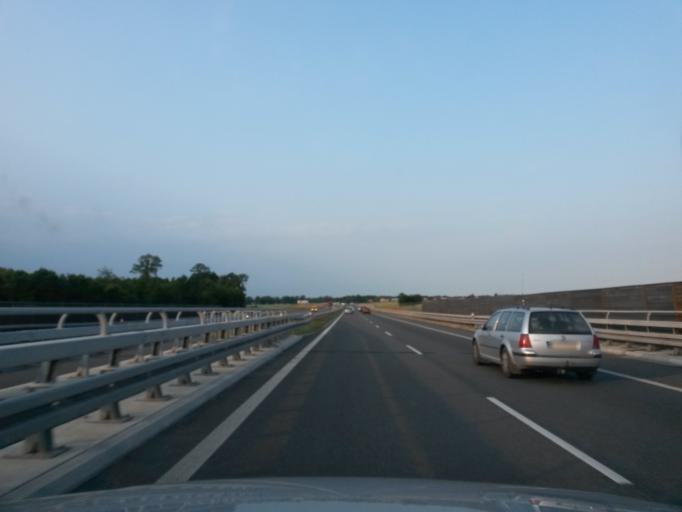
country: PL
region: Lower Silesian Voivodeship
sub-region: Powiat olesnicki
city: Twardogora
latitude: 51.2496
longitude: 17.5224
